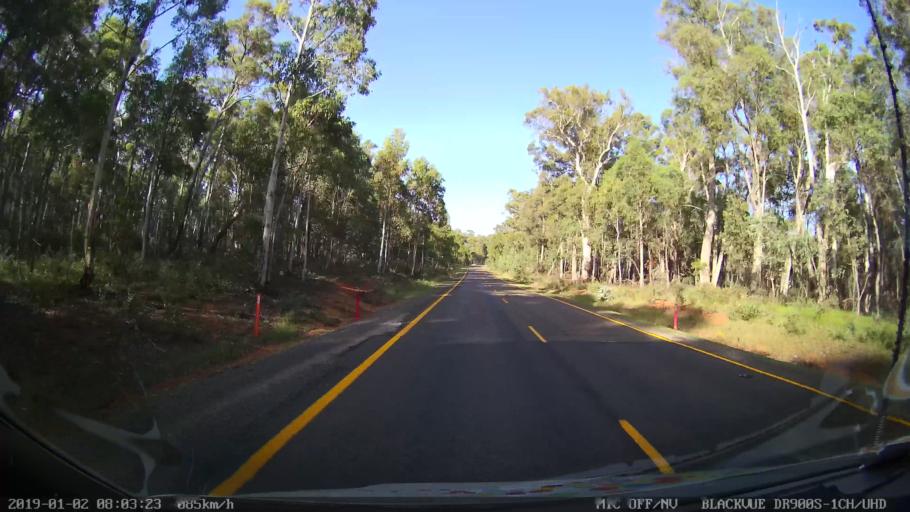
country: AU
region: New South Wales
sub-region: Tumut Shire
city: Tumut
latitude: -35.6623
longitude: 148.4092
